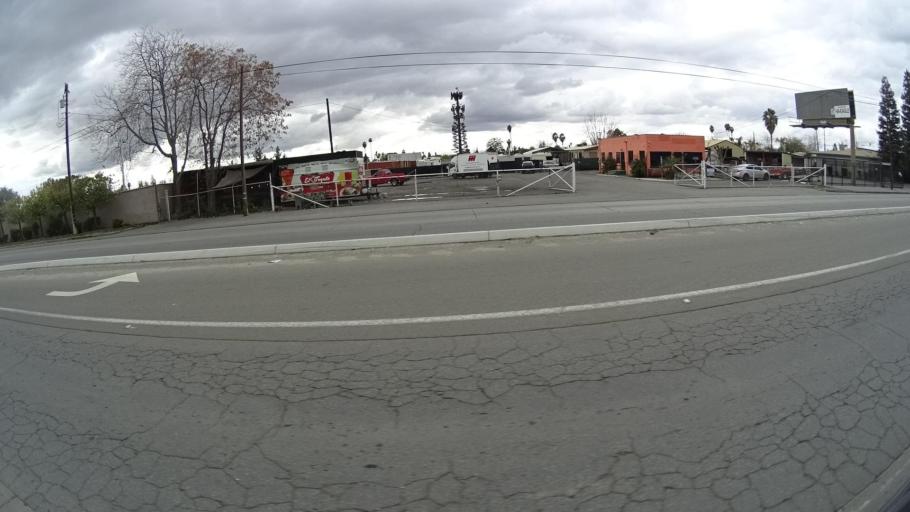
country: US
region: California
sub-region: Kern County
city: Greenfield
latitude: 35.3133
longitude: -119.0030
